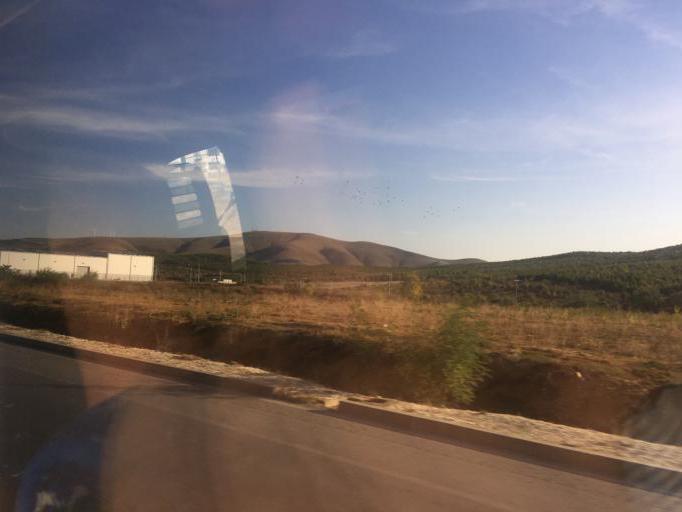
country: XK
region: Pristina
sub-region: Komuna e Drenasit
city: Glogovac
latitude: 42.6011
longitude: 20.9599
